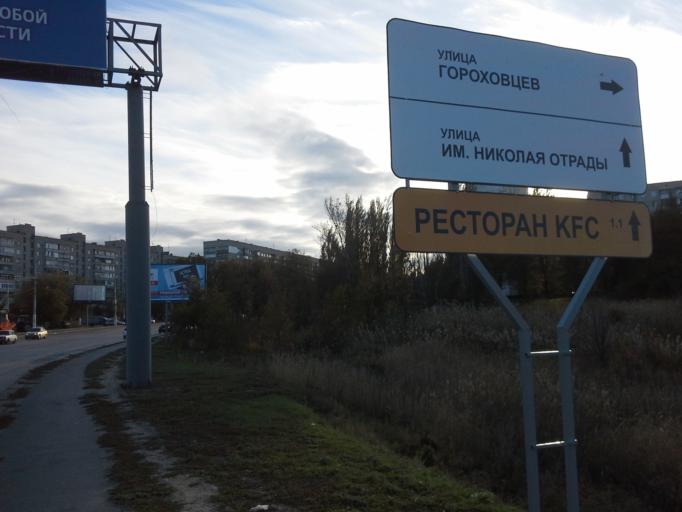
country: RU
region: Volgograd
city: Vodstroy
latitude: 48.8248
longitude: 44.6418
